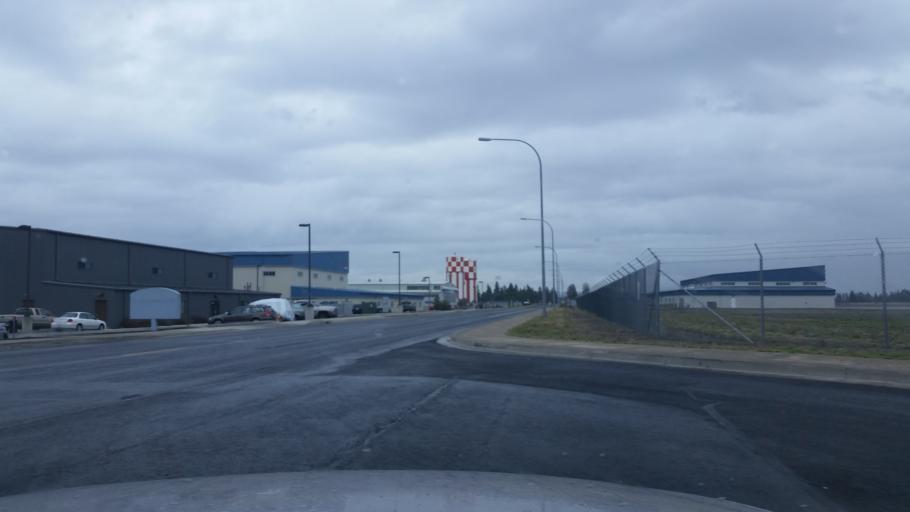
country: US
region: Washington
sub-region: Spokane County
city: Airway Heights
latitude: 47.6195
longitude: -117.5287
